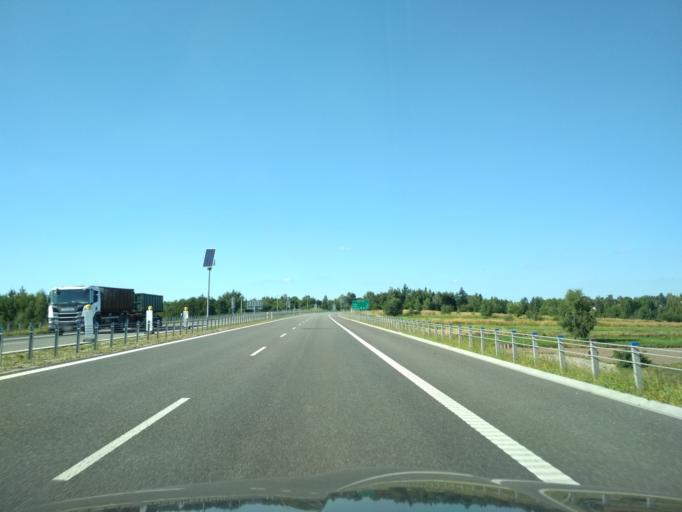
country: PL
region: Subcarpathian Voivodeship
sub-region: Powiat rzeszowski
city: Kielanowka
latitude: 50.0207
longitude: 21.9219
